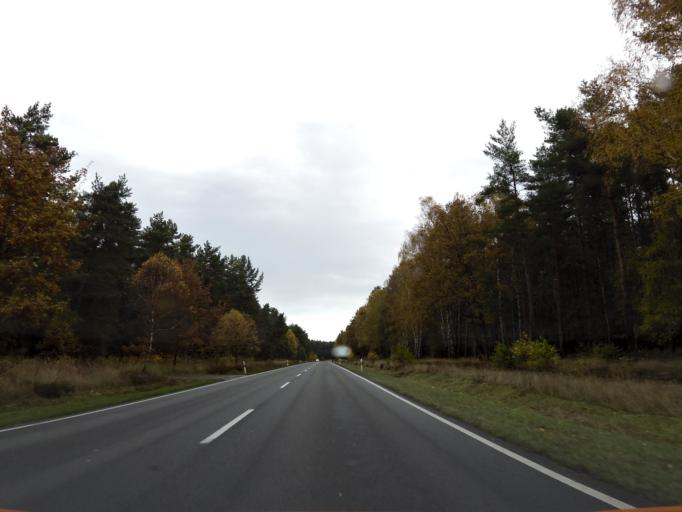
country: DE
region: Saxony-Anhalt
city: Haldensleben I
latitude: 52.3644
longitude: 11.4536
